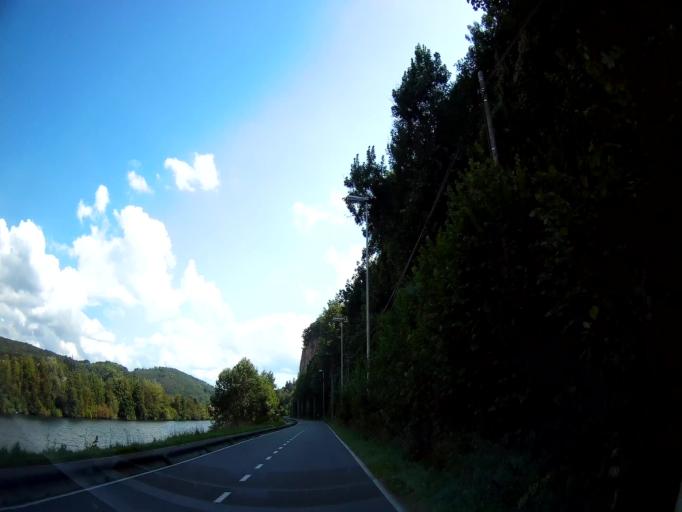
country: BE
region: Wallonia
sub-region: Province de Namur
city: Yvoir
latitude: 50.3434
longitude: 4.8563
